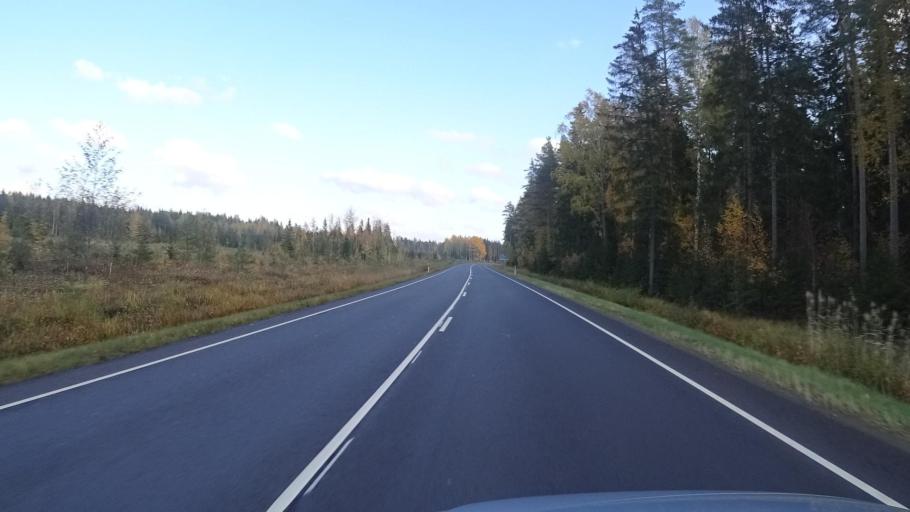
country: FI
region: Satakunta
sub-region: Rauma
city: Eura
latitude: 61.1072
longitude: 22.2176
